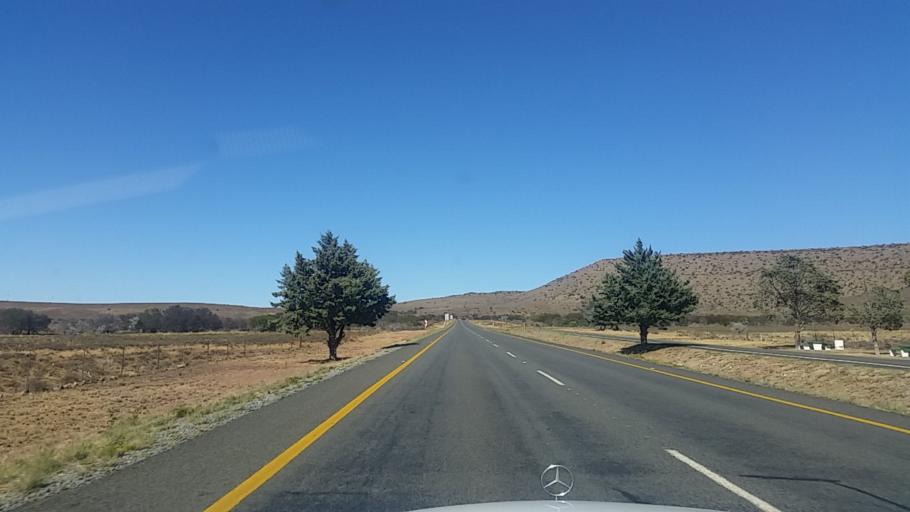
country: ZA
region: Eastern Cape
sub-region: Cacadu District Municipality
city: Graaff-Reinet
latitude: -31.9401
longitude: 24.7335
